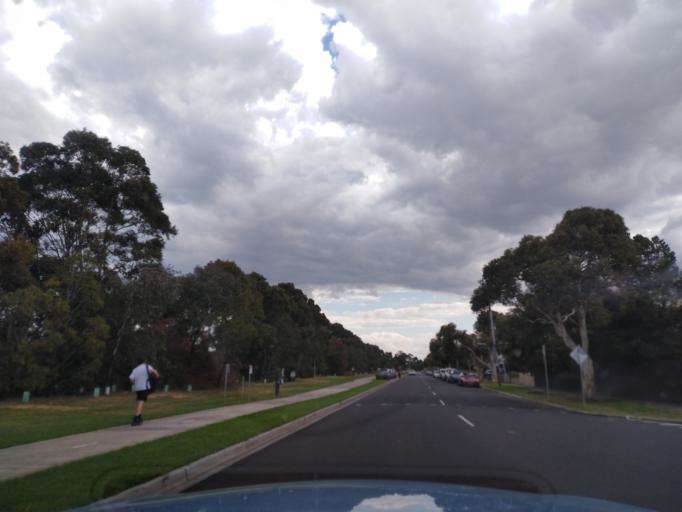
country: AU
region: Victoria
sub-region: Hobsons Bay
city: Newport
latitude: -37.8469
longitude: 144.8798
